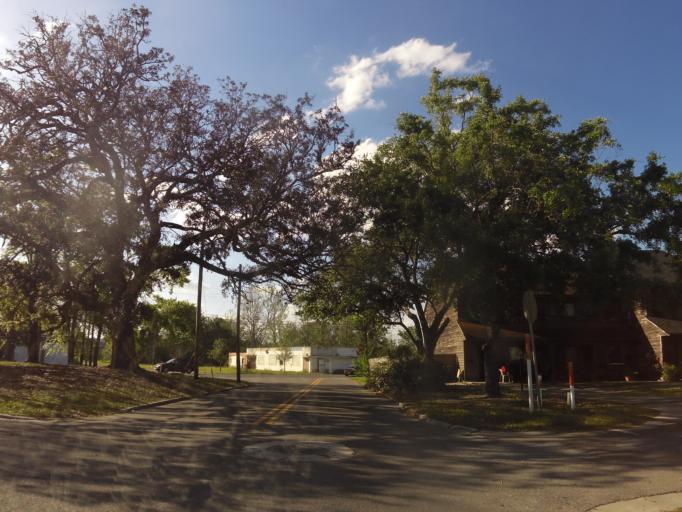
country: US
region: Florida
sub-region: Duval County
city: Jacksonville
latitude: 30.3247
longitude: -81.6775
